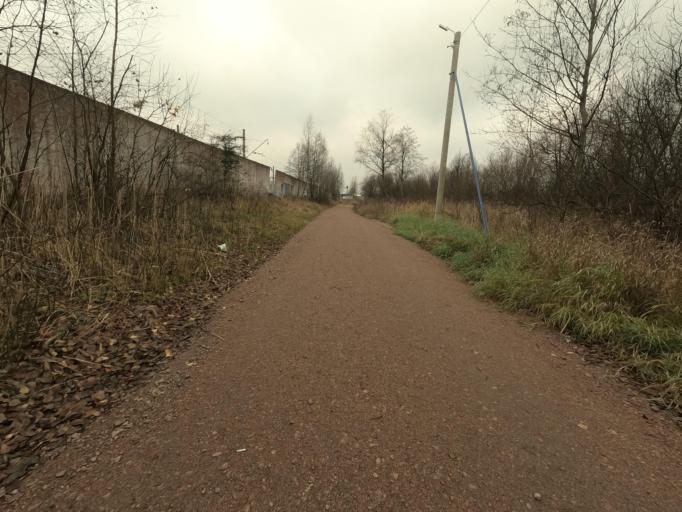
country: RU
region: Leningrad
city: Lyuban'
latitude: 59.4924
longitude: 31.2725
